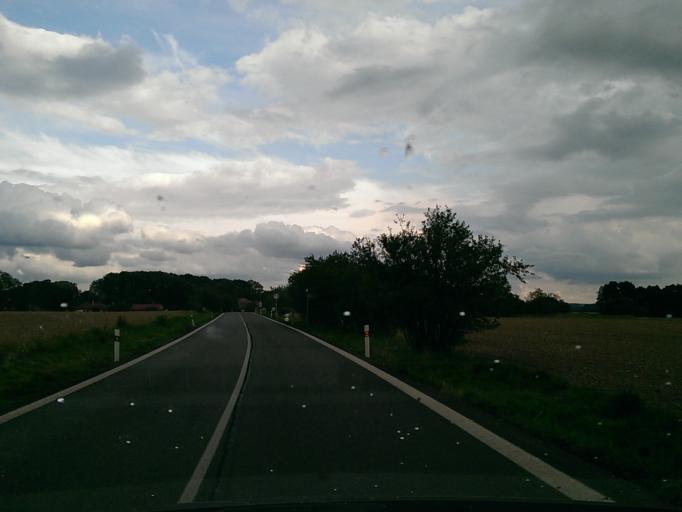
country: CZ
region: Central Bohemia
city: Knezmost
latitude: 50.4826
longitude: 15.0123
